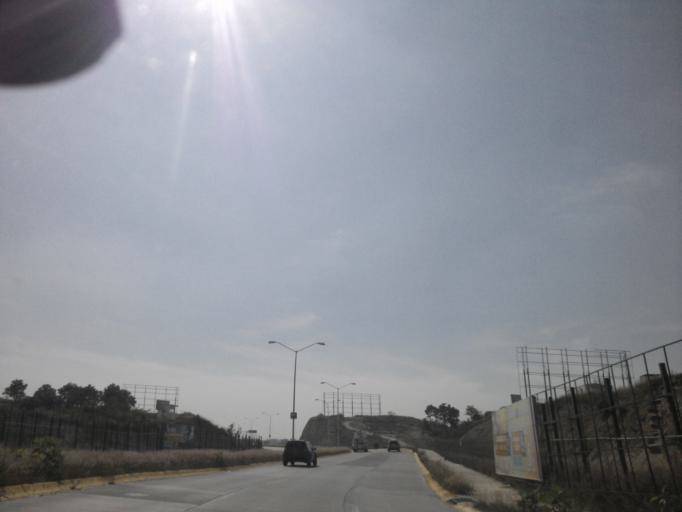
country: MX
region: Jalisco
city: Zapopan2
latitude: 20.7079
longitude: -103.4266
